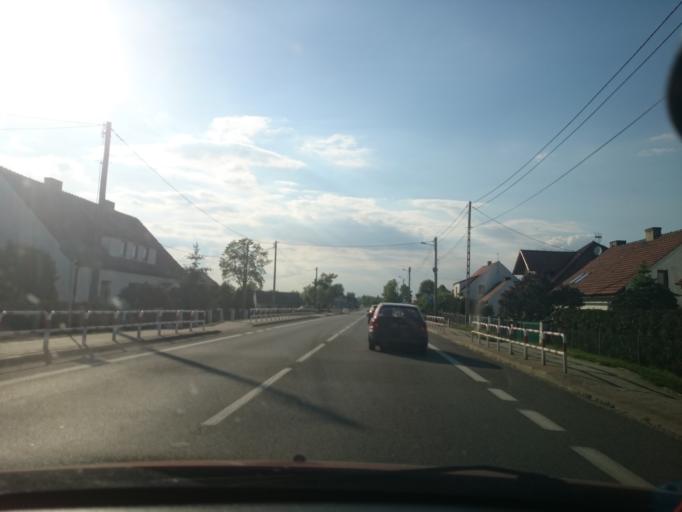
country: PL
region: Opole Voivodeship
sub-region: Powiat strzelecki
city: Izbicko
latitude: 50.5518
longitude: 18.2239
